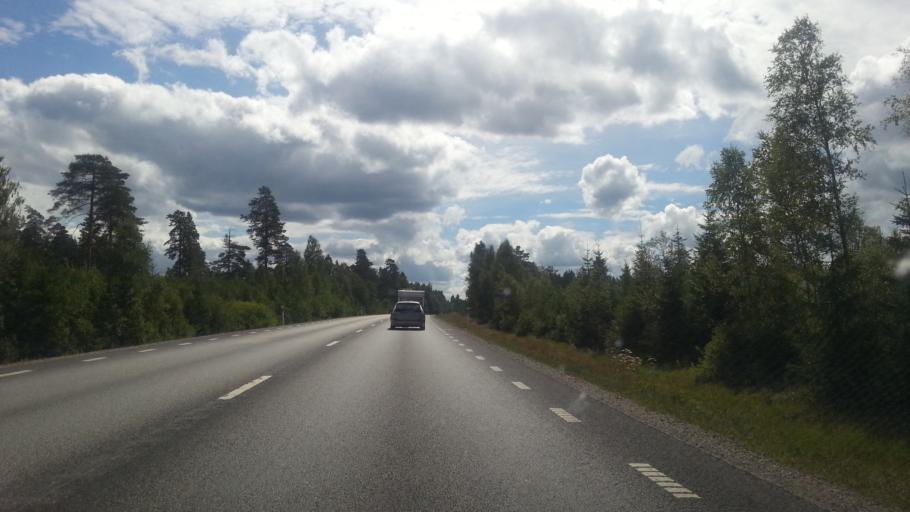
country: SE
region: OErebro
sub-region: Lindesbergs Kommun
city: Lindesberg
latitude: 59.5647
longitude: 15.2166
